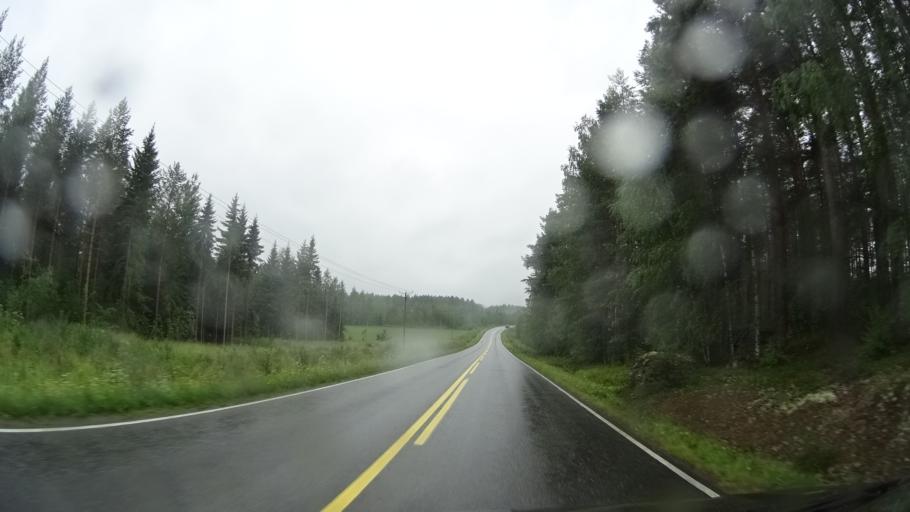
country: FI
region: North Karelia
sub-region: Keski-Karjala
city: Raeaekkylae
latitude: 62.3066
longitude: 29.5769
